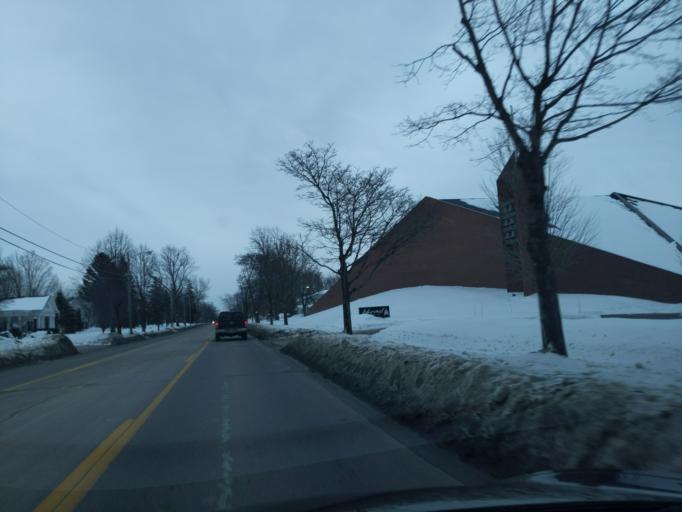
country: US
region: Michigan
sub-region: Ottawa County
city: Spring Lake
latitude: 43.0767
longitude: -86.1945
